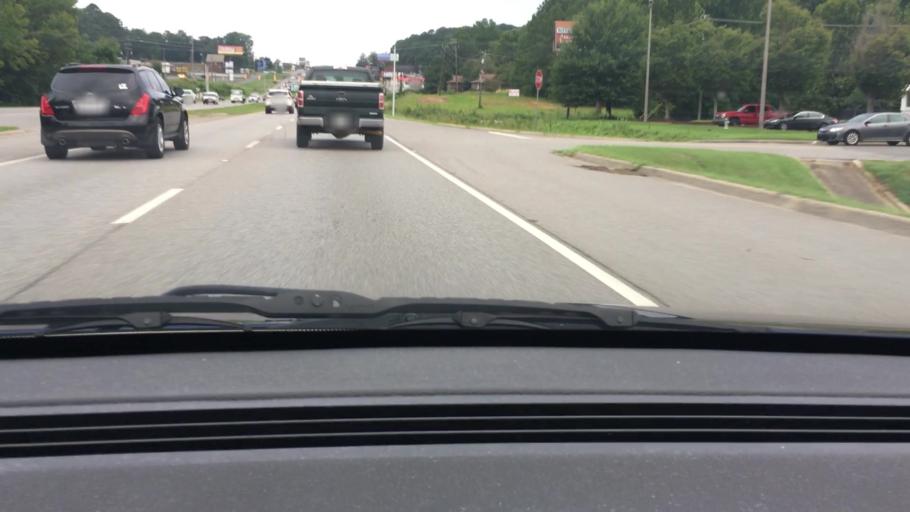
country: US
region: Alabama
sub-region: Tuscaloosa County
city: Northport
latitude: 33.2371
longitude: -87.5623
